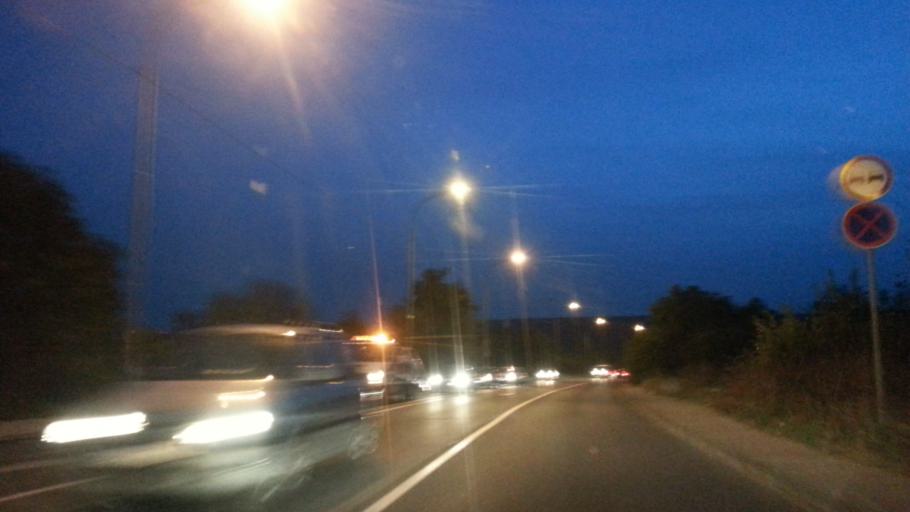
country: RS
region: Central Serbia
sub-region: Belgrade
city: Vozdovac
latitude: 44.7562
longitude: 20.4724
